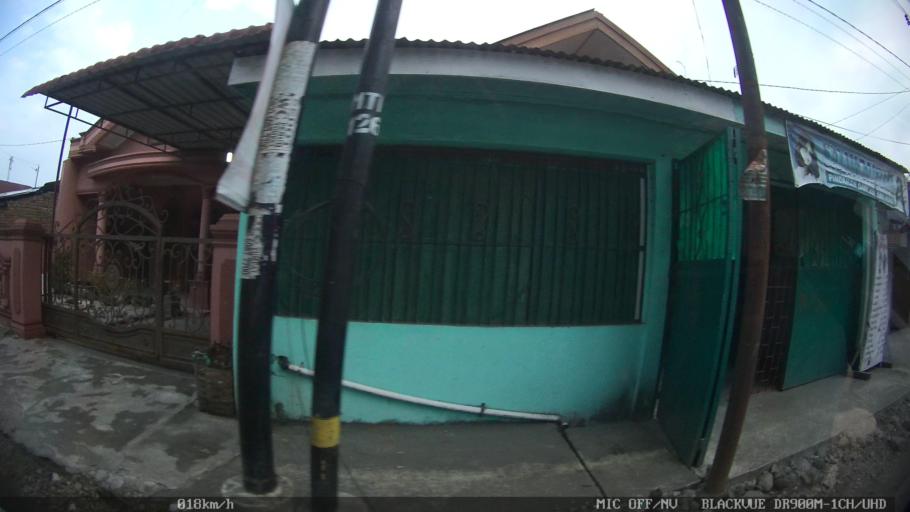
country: ID
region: North Sumatra
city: Medan
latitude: 3.6083
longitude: 98.6839
